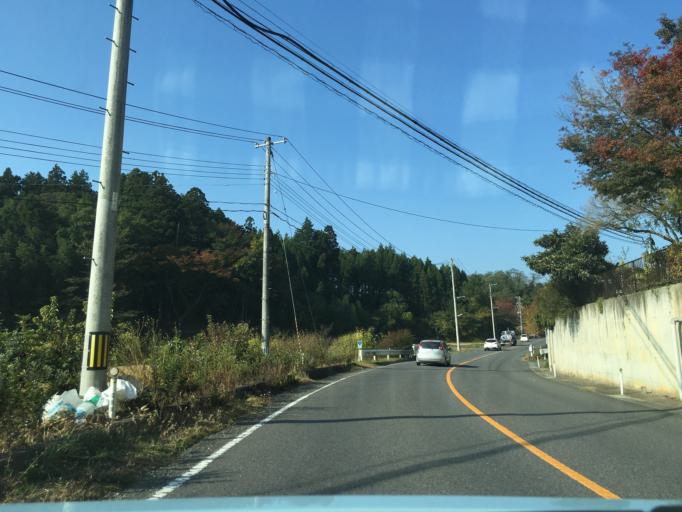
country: JP
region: Fukushima
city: Sukagawa
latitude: 37.2818
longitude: 140.3310
